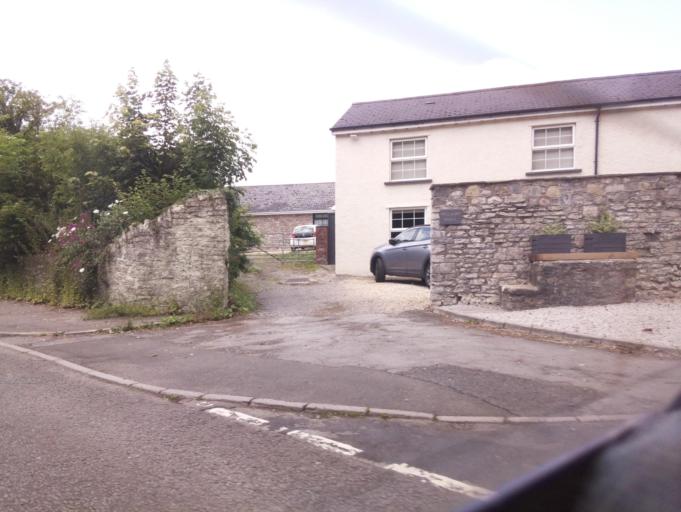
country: GB
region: Wales
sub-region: Vale of Glamorgan
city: Barry
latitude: 51.4597
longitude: -3.3138
